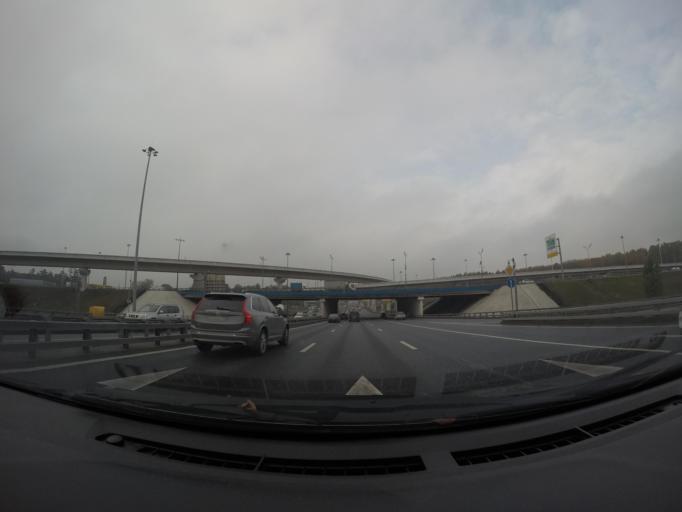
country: RU
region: Moscow
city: Rublevo
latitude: 55.7894
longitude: 37.3743
